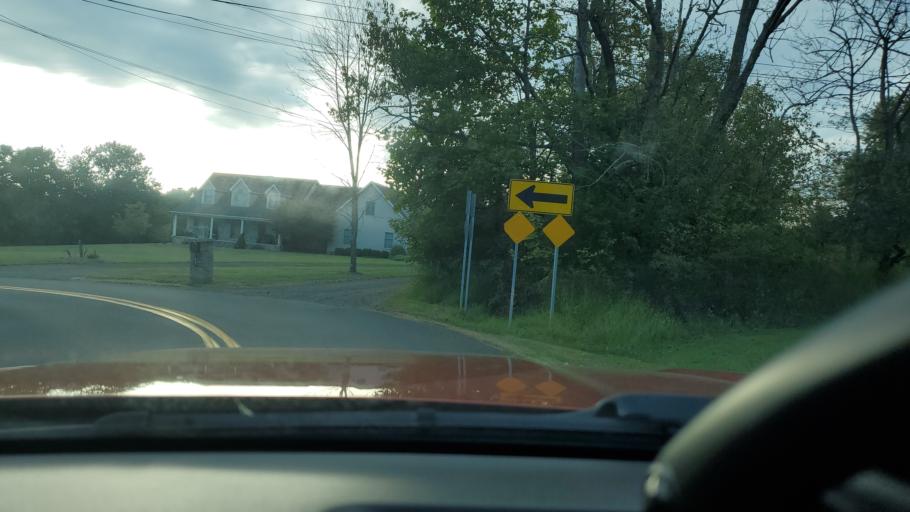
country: US
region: Pennsylvania
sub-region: Montgomery County
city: Woxall
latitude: 40.2992
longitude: -75.4713
